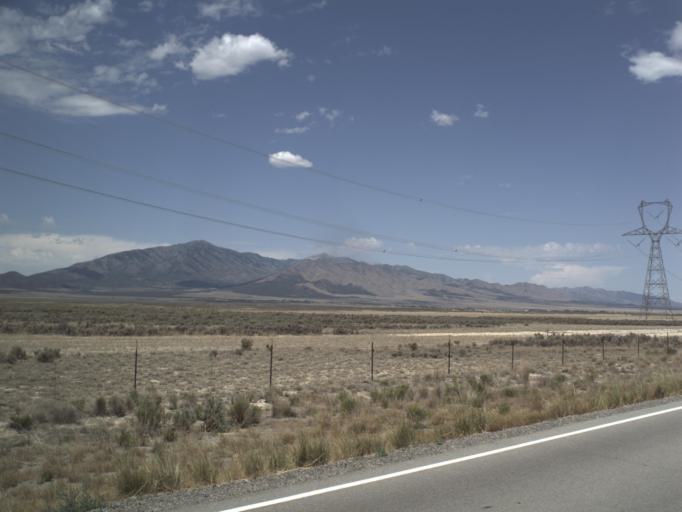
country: US
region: Utah
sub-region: Tooele County
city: Tooele
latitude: 40.2690
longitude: -112.3974
